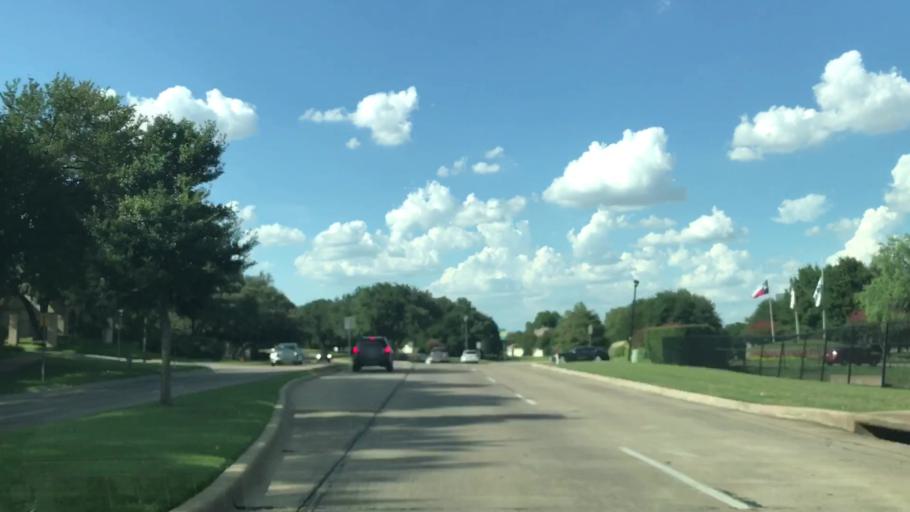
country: US
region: Texas
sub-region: Dallas County
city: Irving
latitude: 32.8585
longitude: -96.9503
